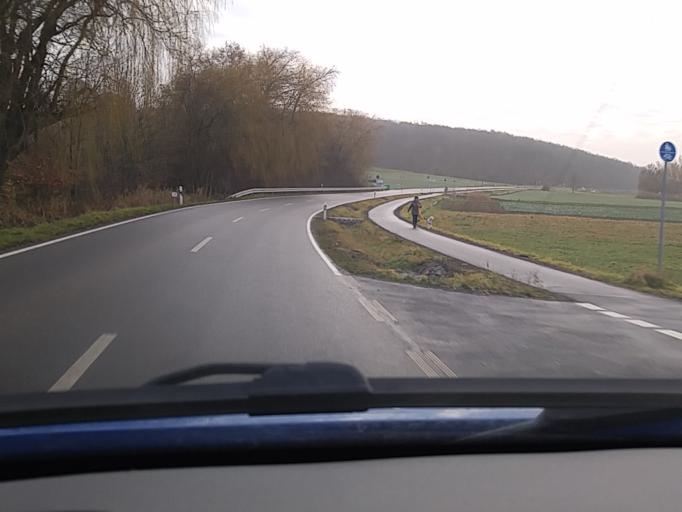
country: DE
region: Hesse
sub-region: Regierungsbezirk Darmstadt
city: Bad Nauheim
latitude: 50.3896
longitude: 8.7548
